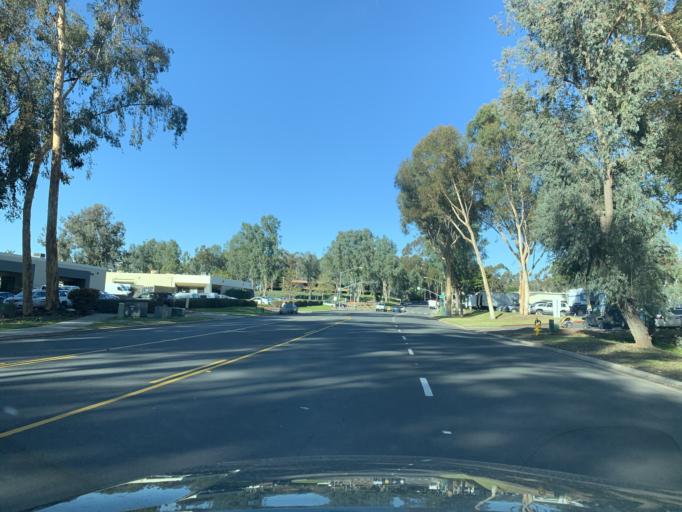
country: US
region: California
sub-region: San Diego County
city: Poway
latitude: 32.9024
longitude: -117.1116
